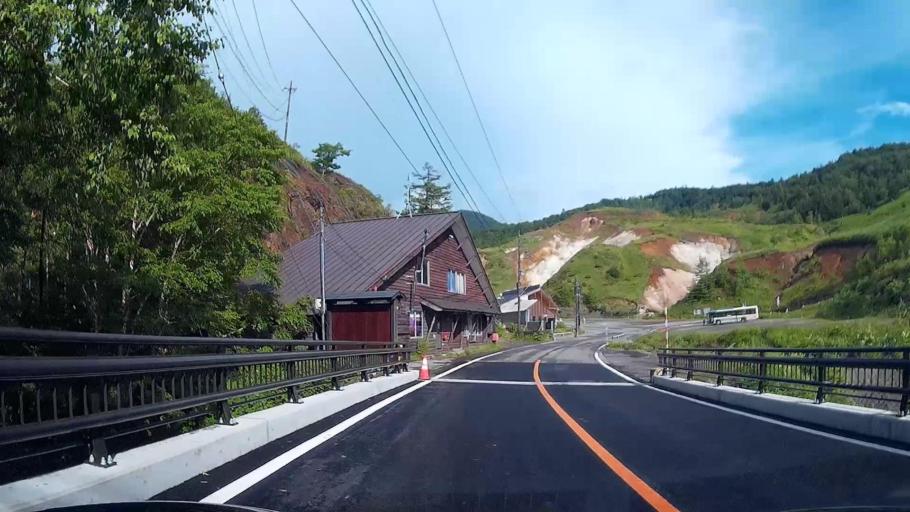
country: JP
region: Nagano
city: Nakano
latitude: 36.6349
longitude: 138.5083
